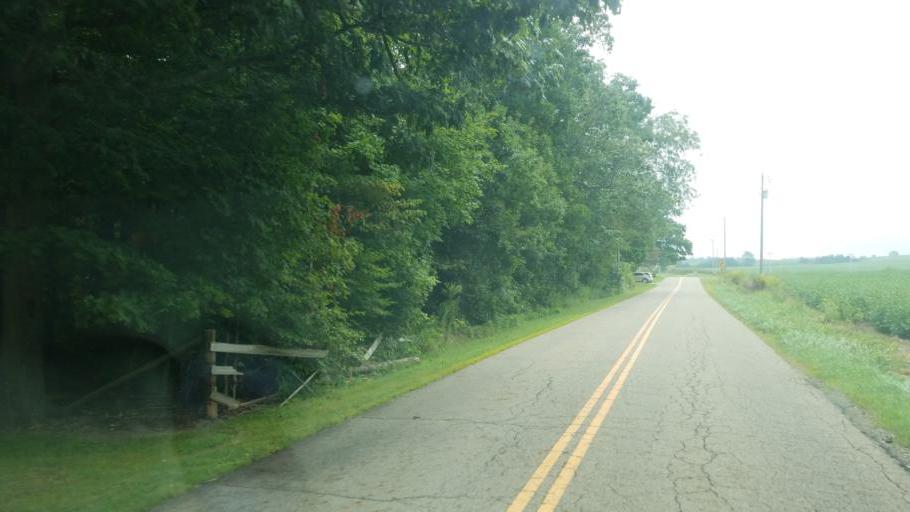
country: US
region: Ohio
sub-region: Licking County
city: Utica
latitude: 40.2981
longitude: -82.4367
